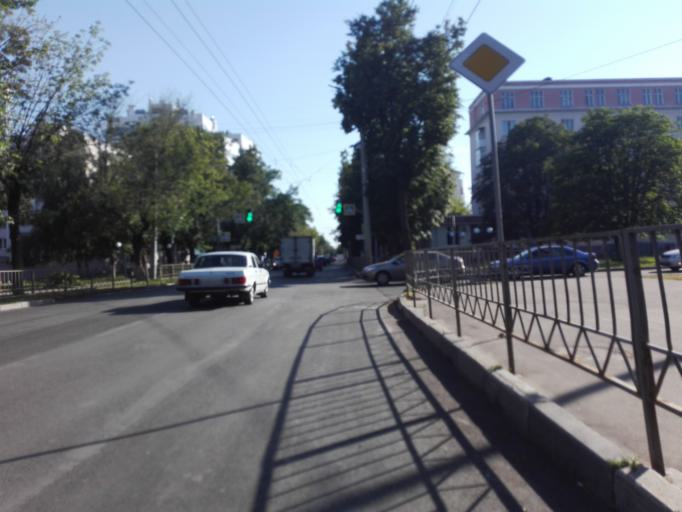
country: RU
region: Orjol
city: Orel
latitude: 52.9734
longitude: 36.0601
